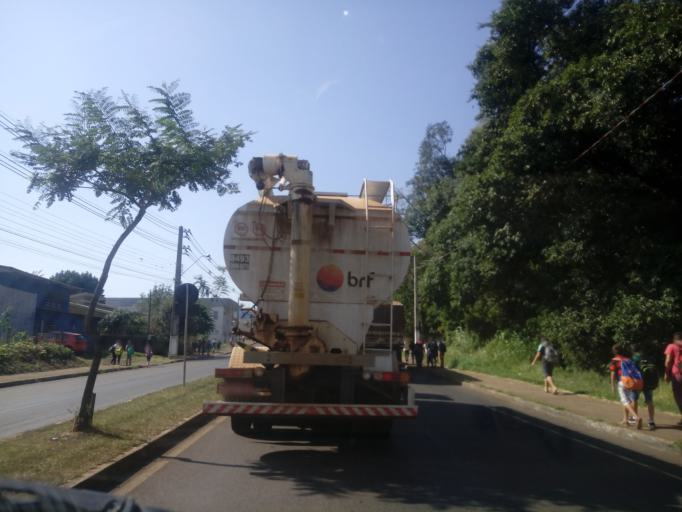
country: BR
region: Santa Catarina
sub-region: Chapeco
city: Chapeco
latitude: -27.0899
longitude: -52.6798
